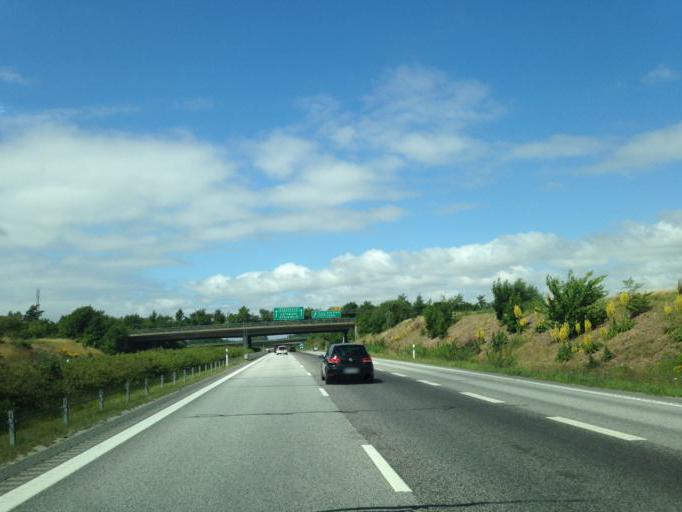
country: SE
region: Skane
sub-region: Burlovs Kommun
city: Arloev
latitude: 55.6353
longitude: 13.1075
